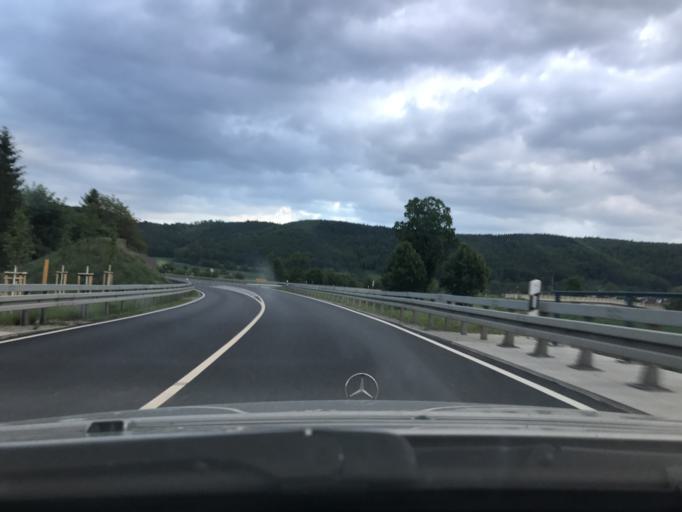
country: DE
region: Hesse
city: Wanfried
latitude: 51.1889
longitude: 10.1232
